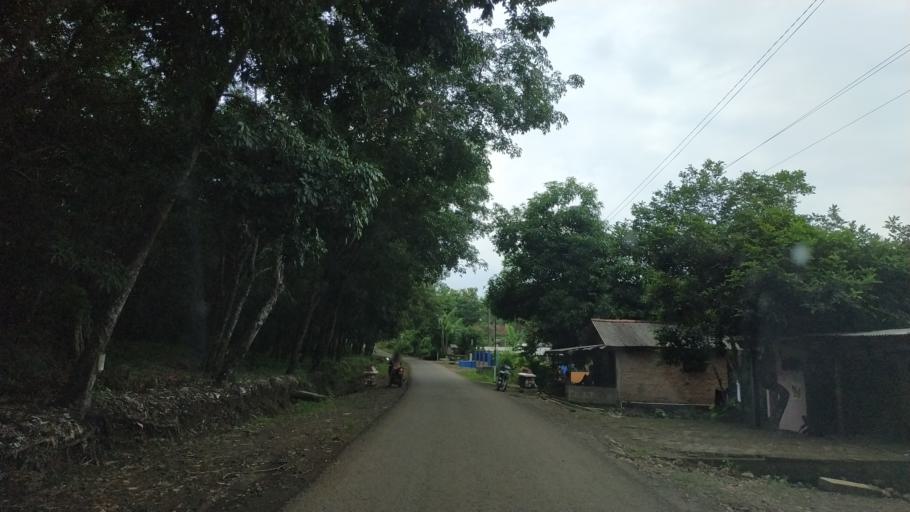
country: ID
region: Central Java
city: Krajan Tegalombo
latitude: -6.4326
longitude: 110.9829
